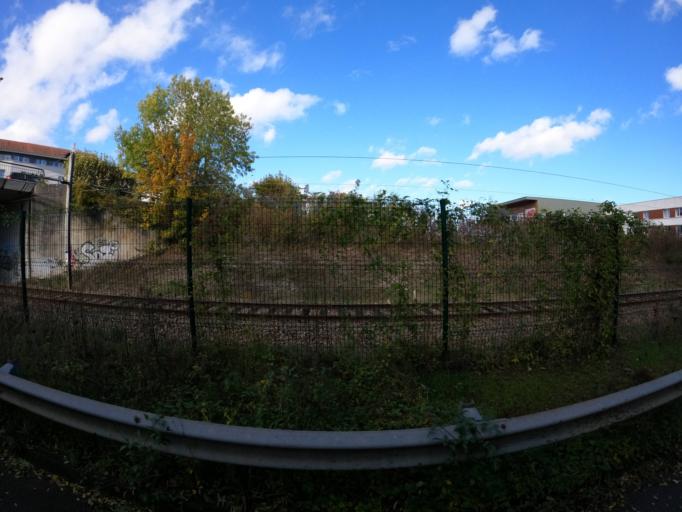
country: FR
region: Ile-de-France
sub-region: Departement de Seine-et-Marne
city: Esbly
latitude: 48.8965
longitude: 2.8111
